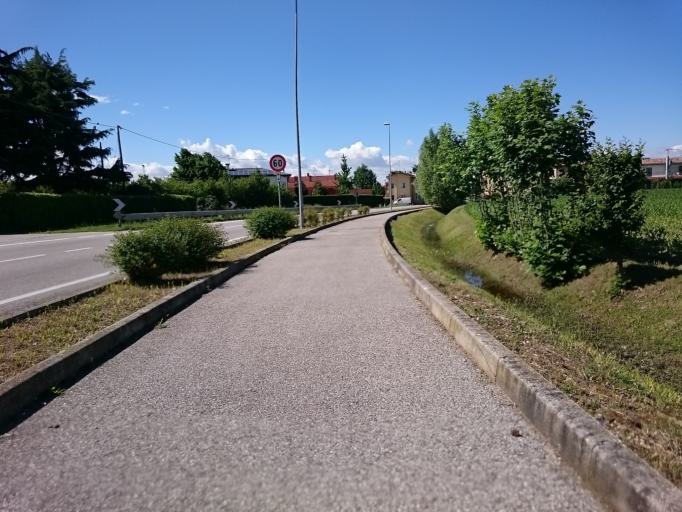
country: IT
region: Veneto
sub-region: Provincia di Venezia
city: Campolongo Maggiore Liettoli
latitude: 45.3240
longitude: 12.0262
